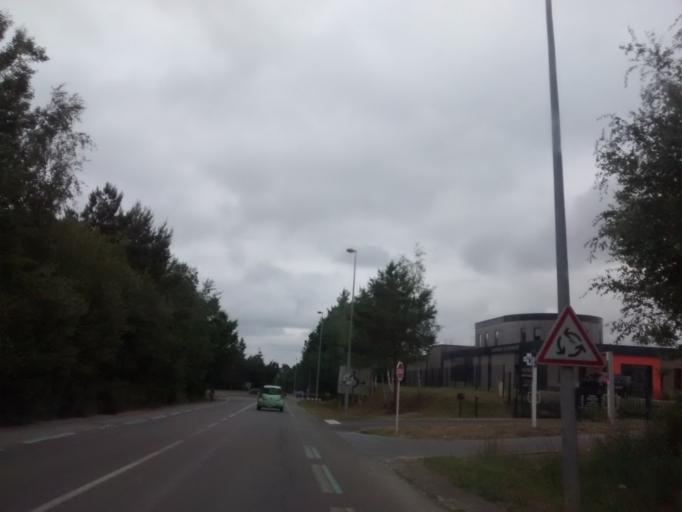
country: FR
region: Brittany
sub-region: Departement d'Ille-et-Vilaine
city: Saint-Gregoire
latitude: 48.1618
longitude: -1.6763
